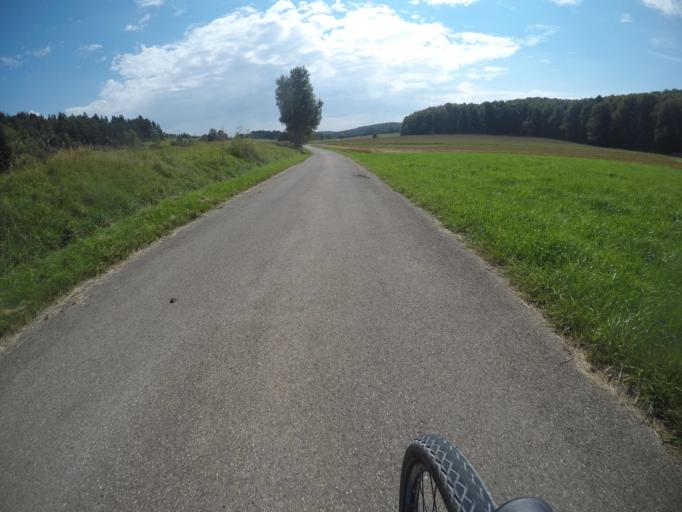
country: DE
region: Baden-Wuerttemberg
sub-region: Tuebingen Region
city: Munsingen
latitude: 48.3890
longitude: 9.5088
